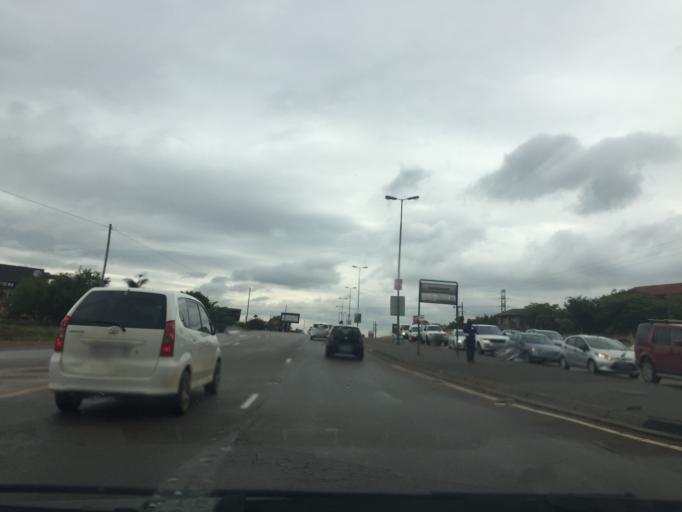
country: ZA
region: Gauteng
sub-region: City of Tshwane Metropolitan Municipality
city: Pretoria
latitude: -25.7785
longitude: 28.3444
